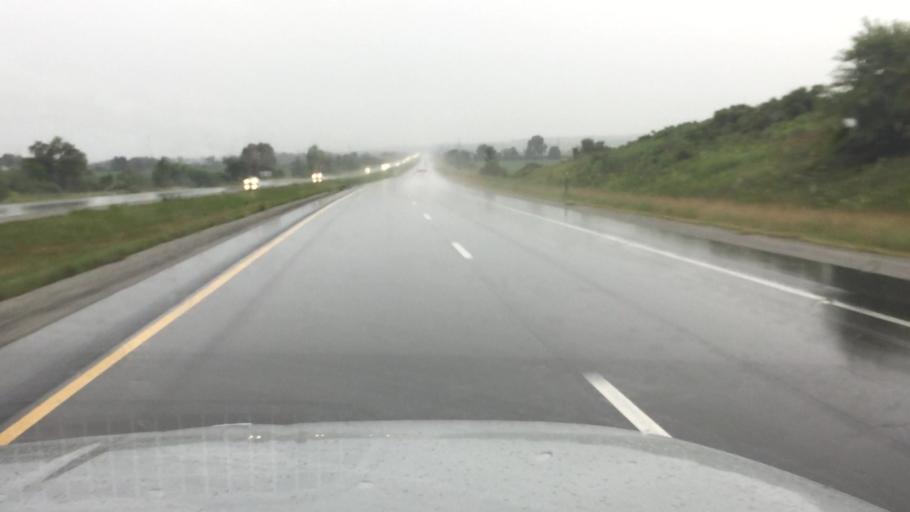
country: US
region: Iowa
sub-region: Johnson County
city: University Heights
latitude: 41.5907
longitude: -91.5459
